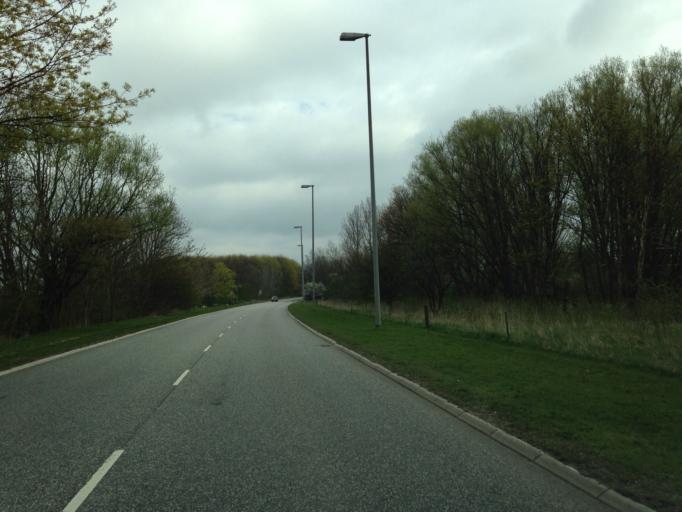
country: DK
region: Capital Region
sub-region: Ishoj Kommune
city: Ishoj
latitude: 55.6076
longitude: 12.3281
